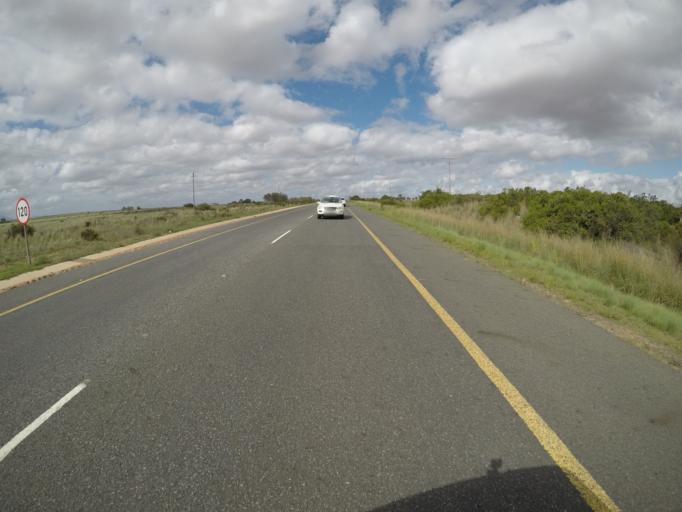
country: ZA
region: Western Cape
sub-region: Eden District Municipality
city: Riversdale
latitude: -34.1704
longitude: 21.3481
